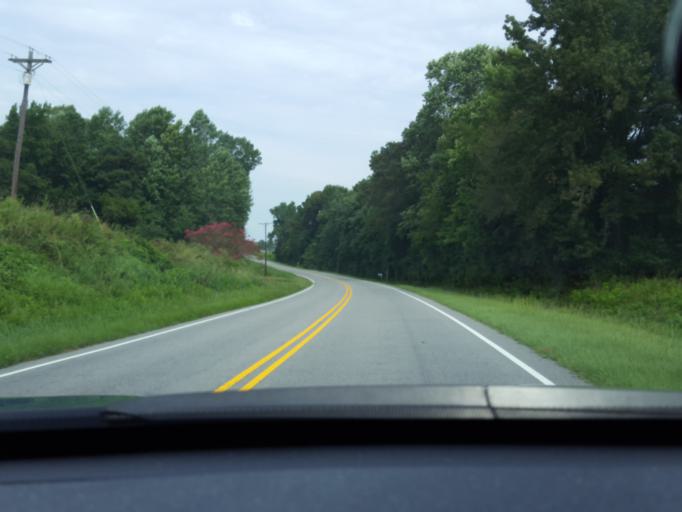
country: US
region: North Carolina
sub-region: Chowan County
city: Edenton
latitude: 36.1713
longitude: -76.6595
